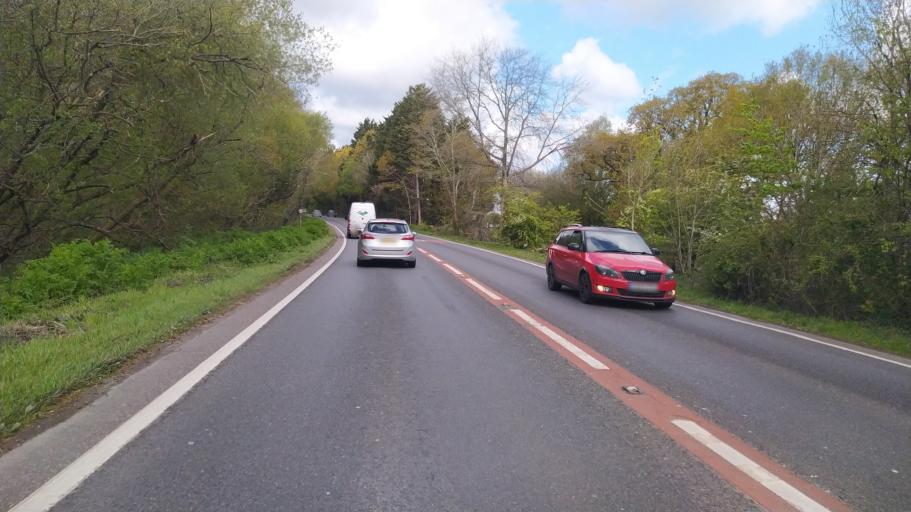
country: GB
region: England
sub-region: Hampshire
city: Marchwood
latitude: 50.8837
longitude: -1.4475
